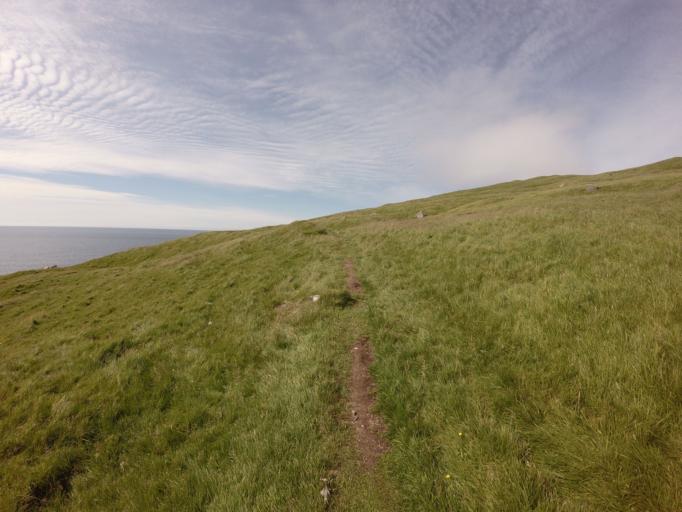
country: FO
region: Vagar
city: Sorvagur
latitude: 62.0998
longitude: -7.6685
